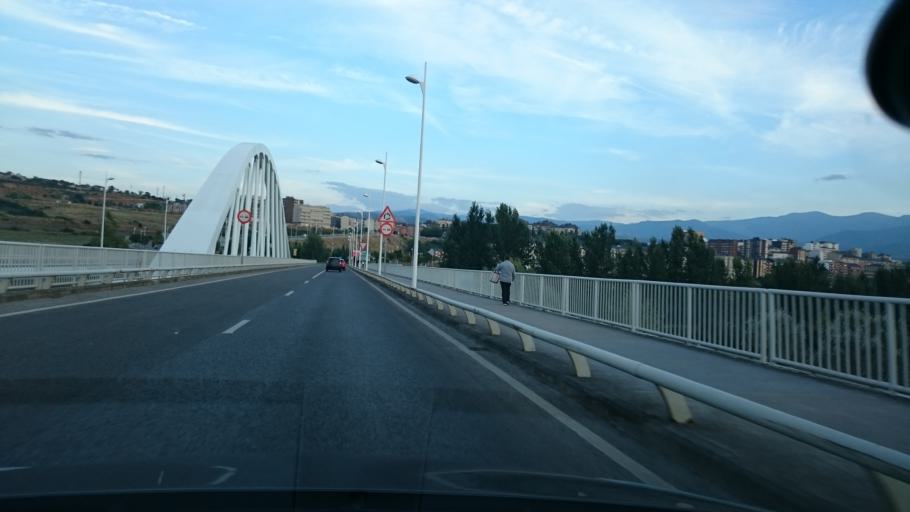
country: ES
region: Castille and Leon
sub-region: Provincia de Leon
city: Ponferrada
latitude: 42.5568
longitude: -6.5914
